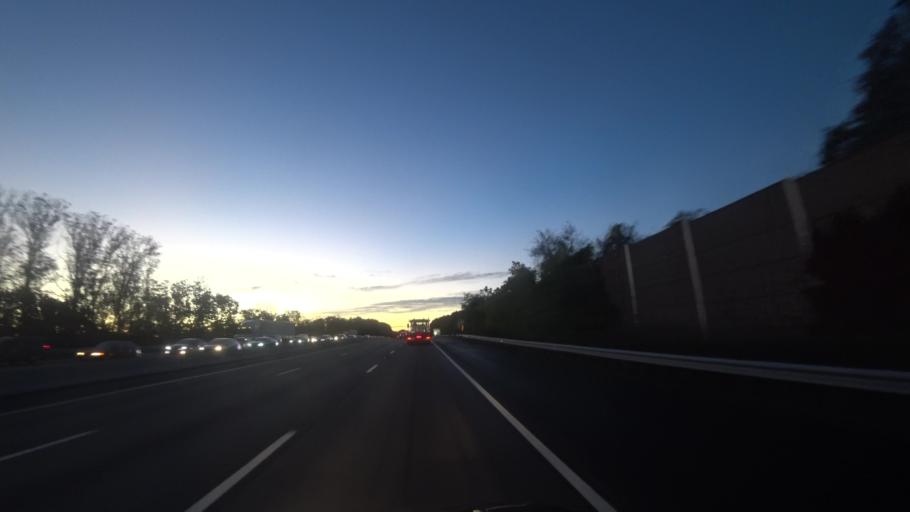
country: US
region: Massachusetts
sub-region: Essex County
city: Lynnfield
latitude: 42.5236
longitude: -71.0602
